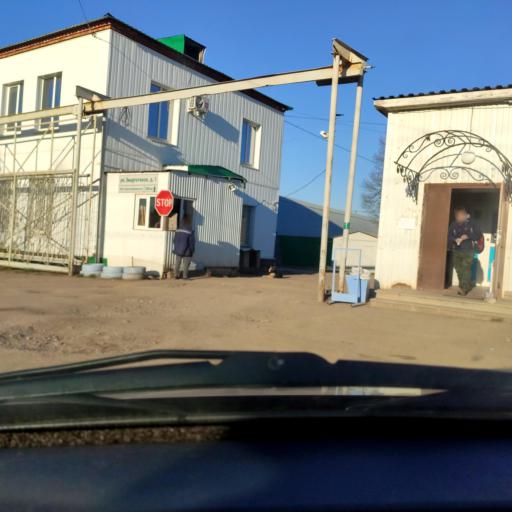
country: RU
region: Bashkortostan
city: Blagoveshchensk
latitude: 54.8955
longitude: 56.0542
